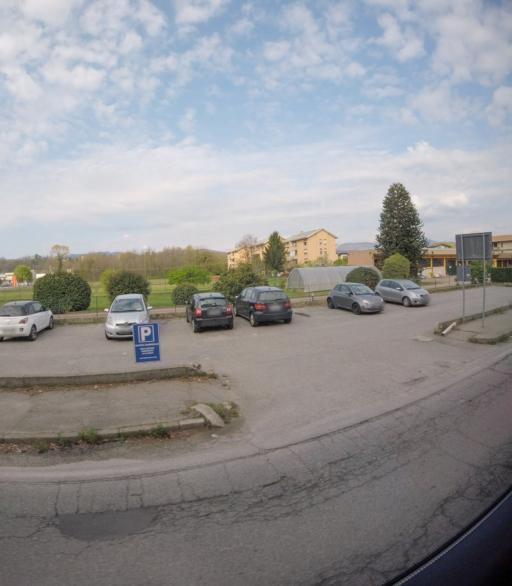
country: IT
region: Piedmont
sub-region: Provincia di Novara
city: Briga Novarese
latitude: 45.7300
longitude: 8.4439
